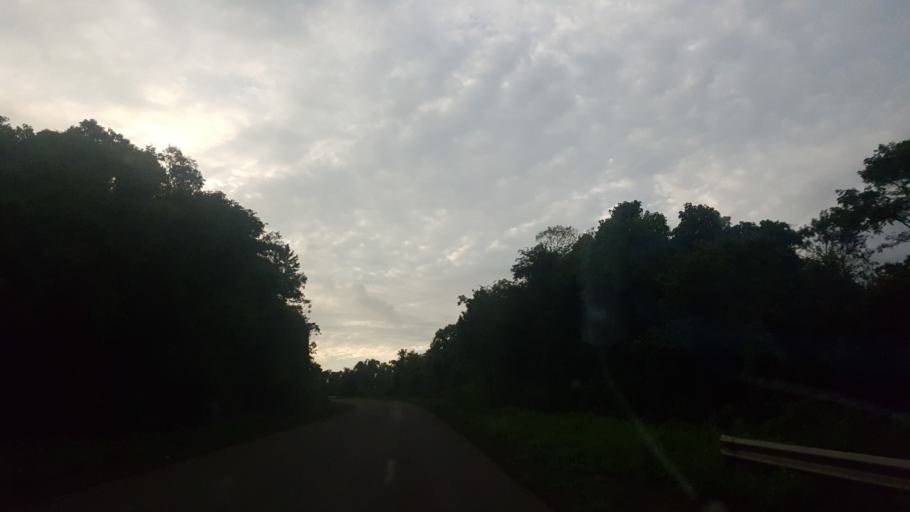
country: AR
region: Misiones
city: Dos de Mayo
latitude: -26.9247
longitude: -54.7268
